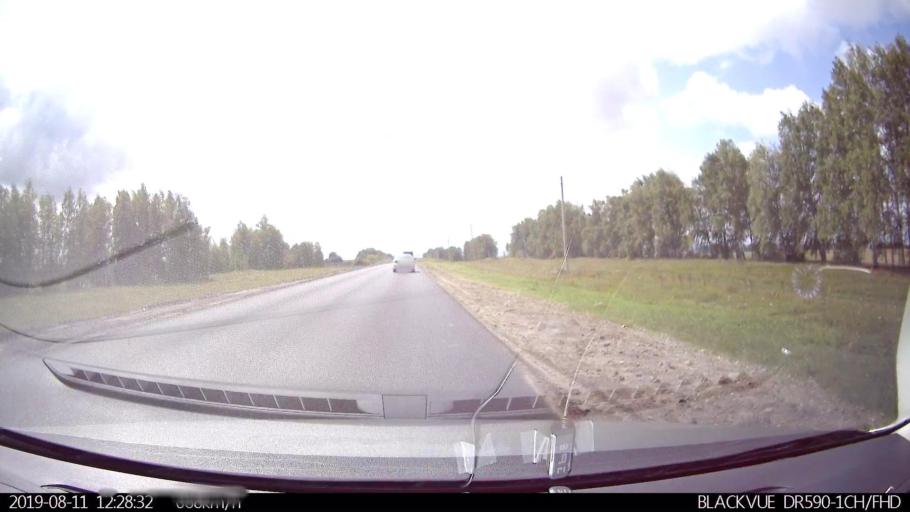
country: RU
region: Ulyanovsk
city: Ignatovka
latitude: 53.8434
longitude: 47.9111
